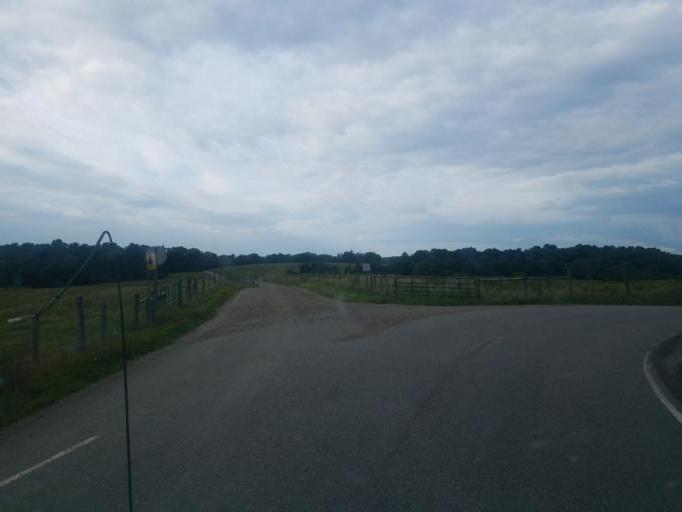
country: US
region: Ohio
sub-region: Knox County
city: Oak Hill
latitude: 40.4118
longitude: -82.1034
